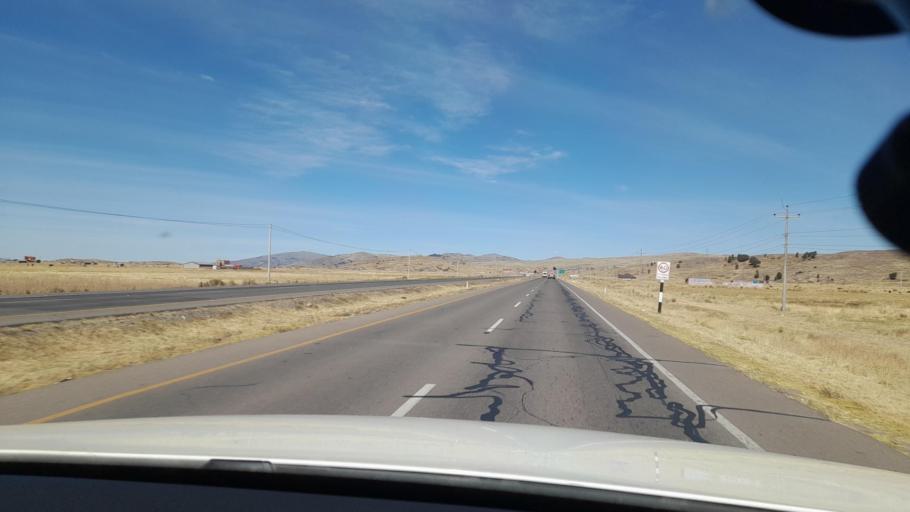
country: PE
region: Puno
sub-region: Provincia de Puno
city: Paucarcolla
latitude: -15.7231
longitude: -70.0607
